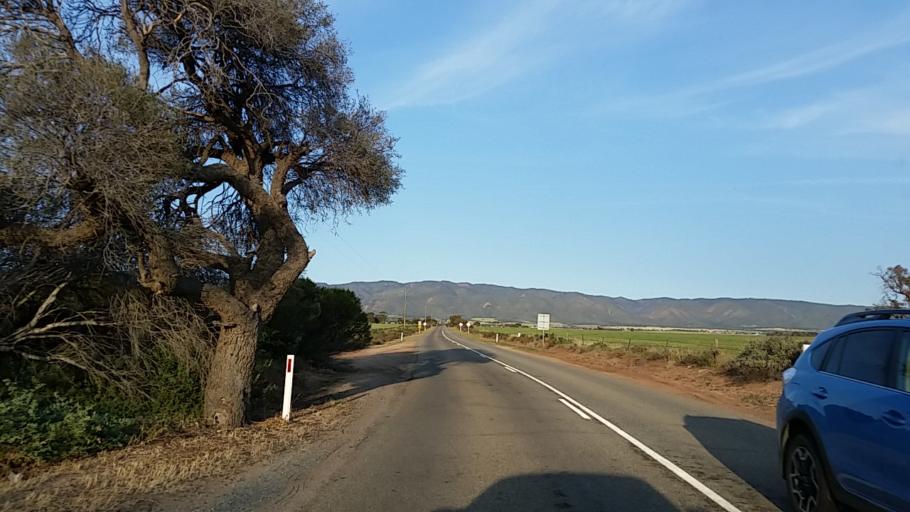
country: AU
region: South Australia
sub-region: Port Pirie City and Dists
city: Port Pirie
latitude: -33.1040
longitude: 138.0563
